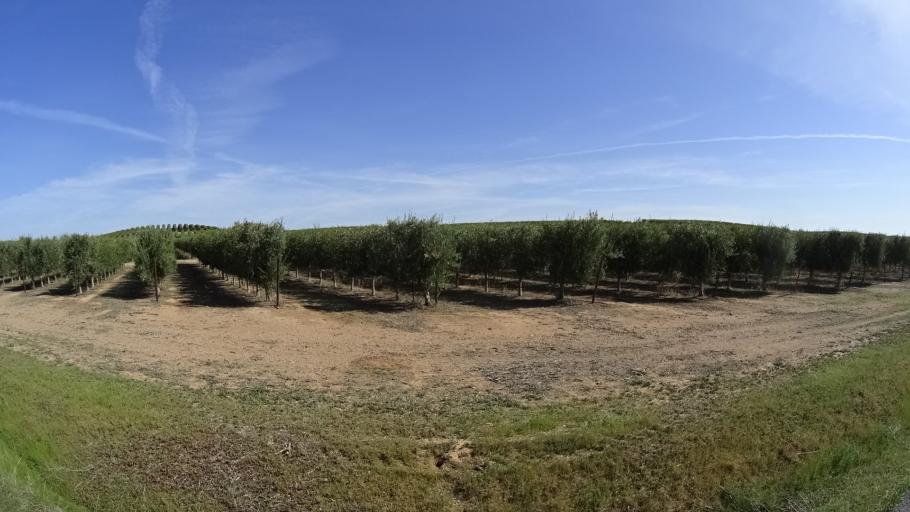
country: US
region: California
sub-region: Glenn County
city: Willows
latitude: 39.6146
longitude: -122.2921
